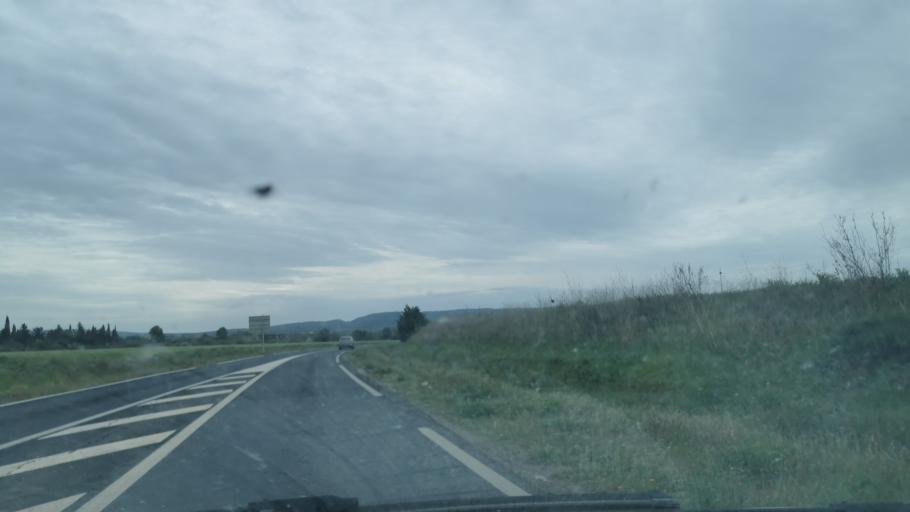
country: FR
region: Languedoc-Roussillon
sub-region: Departement de l'Herault
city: Montbazin
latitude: 43.5132
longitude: 3.6782
